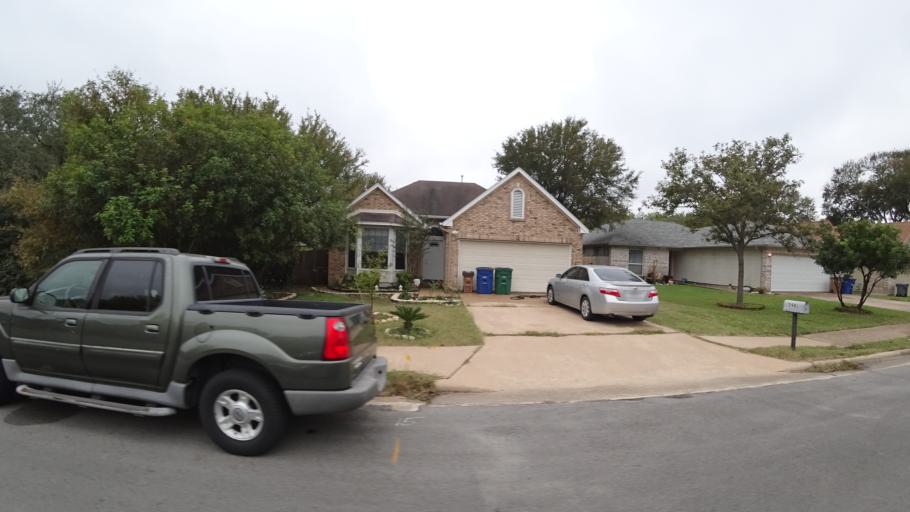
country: US
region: Texas
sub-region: Travis County
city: Shady Hollow
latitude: 30.2054
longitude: -97.8423
